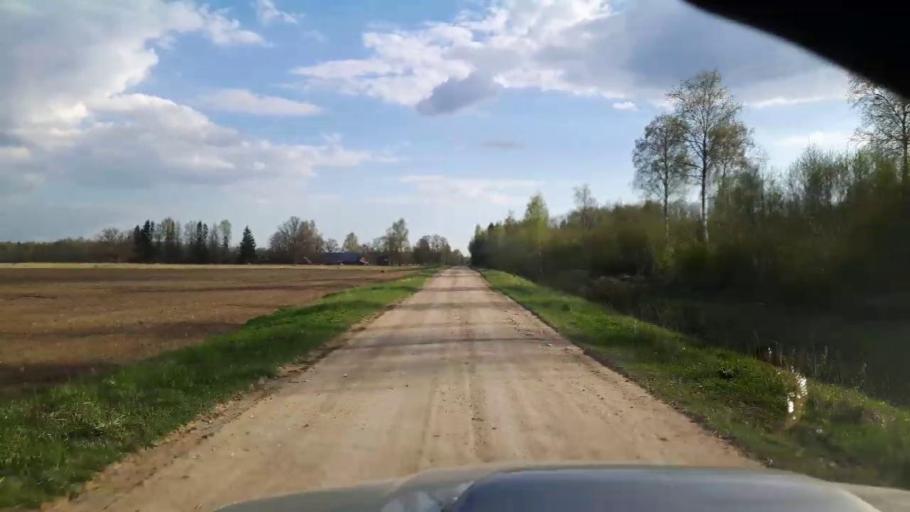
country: EE
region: Paernumaa
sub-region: Tootsi vald
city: Tootsi
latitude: 58.4393
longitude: 24.8104
